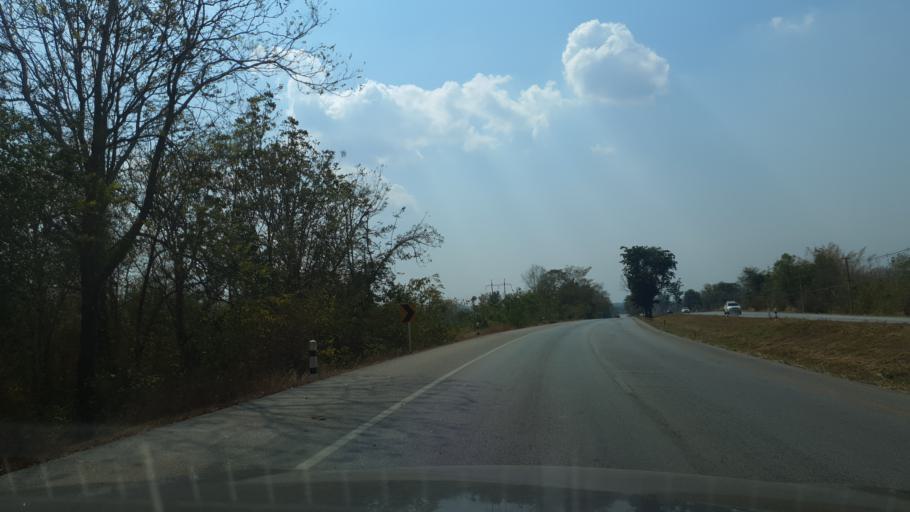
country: TH
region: Lampang
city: Mae Phrik
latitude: 17.4173
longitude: 99.1566
